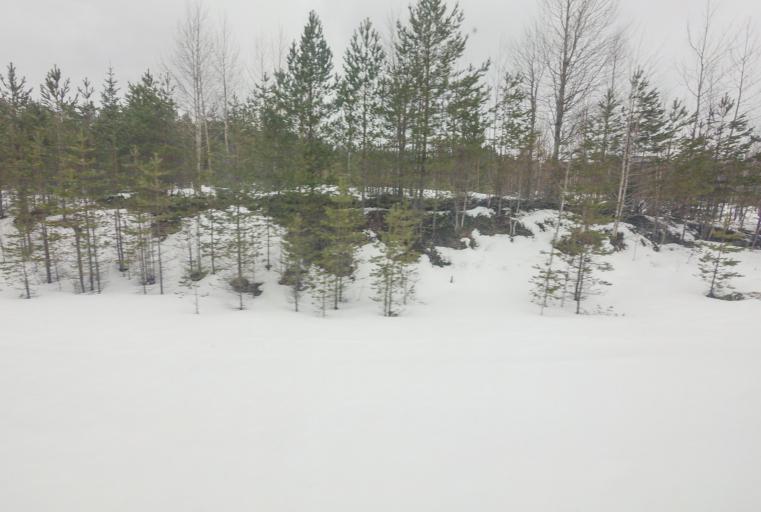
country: FI
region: Southern Savonia
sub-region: Savonlinna
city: Punkaharju
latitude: 61.6570
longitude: 29.4168
